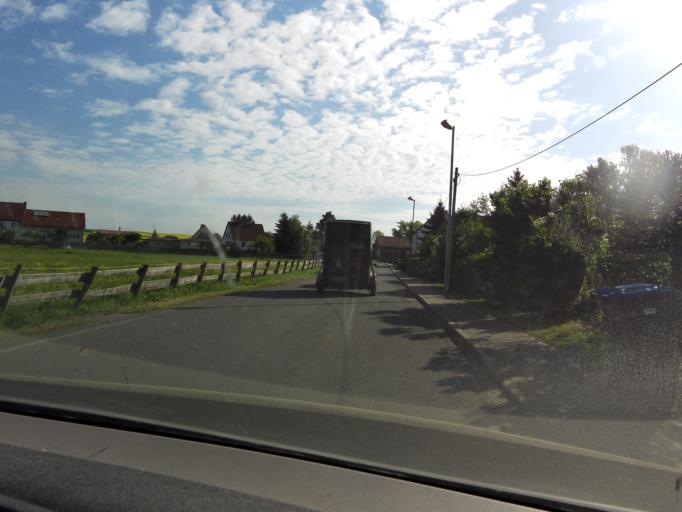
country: DE
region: Thuringia
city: Mechterstadt
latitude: 50.9549
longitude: 10.4993
